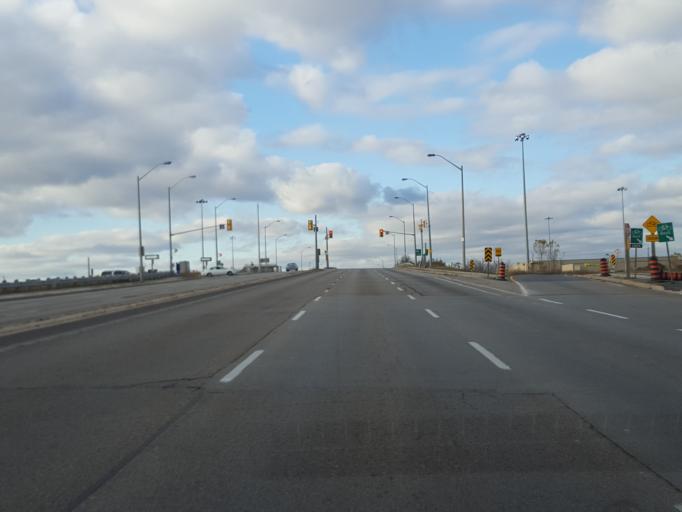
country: CA
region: Ontario
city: Burlington
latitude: 43.3646
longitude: -79.7855
